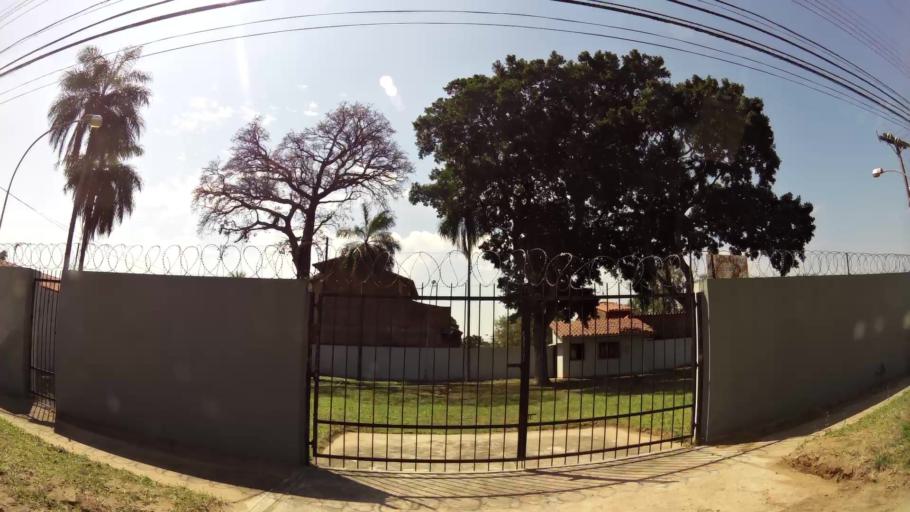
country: BO
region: Santa Cruz
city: Santa Cruz de la Sierra
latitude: -17.7453
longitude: -63.1580
